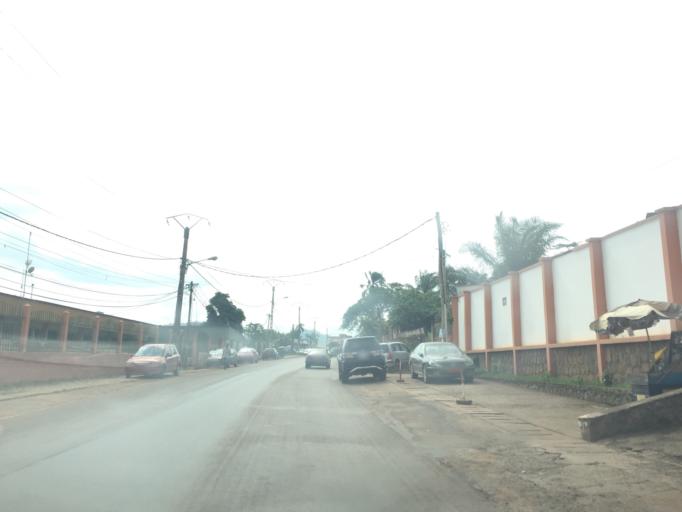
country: CM
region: Centre
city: Yaounde
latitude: 3.8759
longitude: 11.5212
